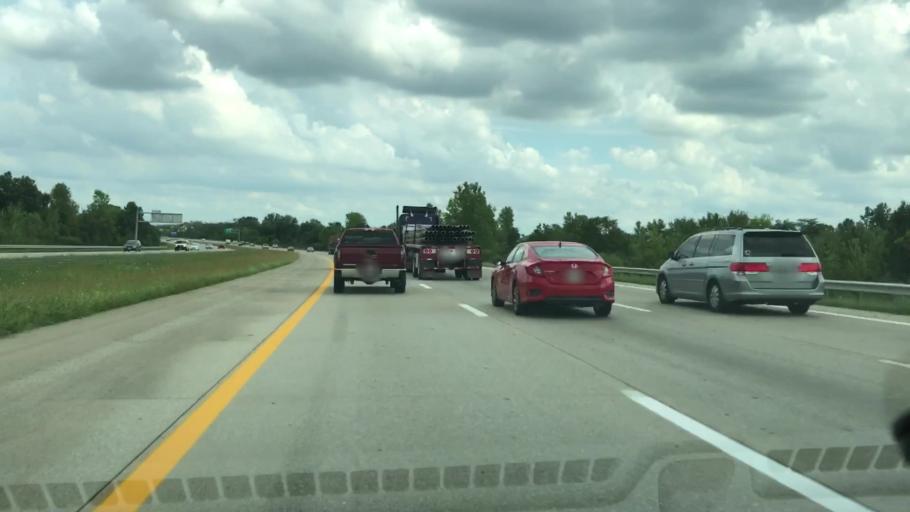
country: US
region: Ohio
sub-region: Franklin County
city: Grove City
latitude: 39.9105
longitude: -83.1060
